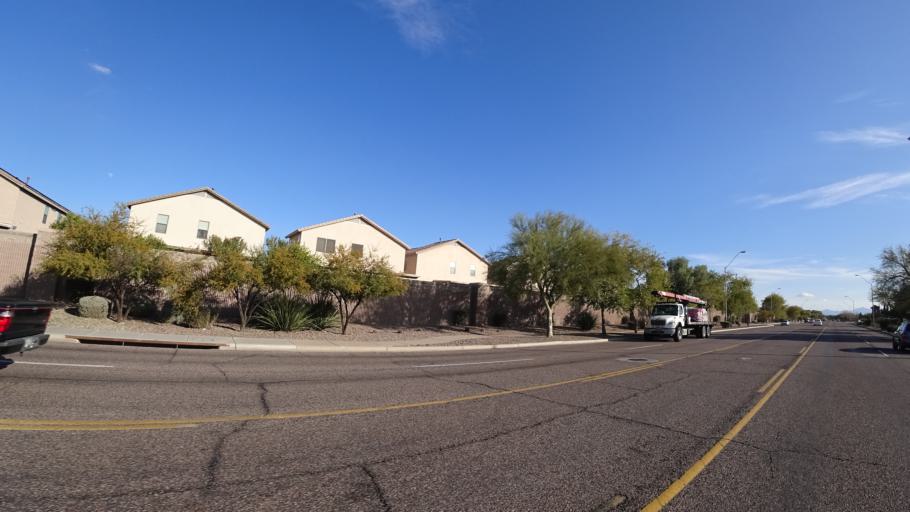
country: US
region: Arizona
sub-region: Maricopa County
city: Sun City
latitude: 33.6508
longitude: -112.2551
